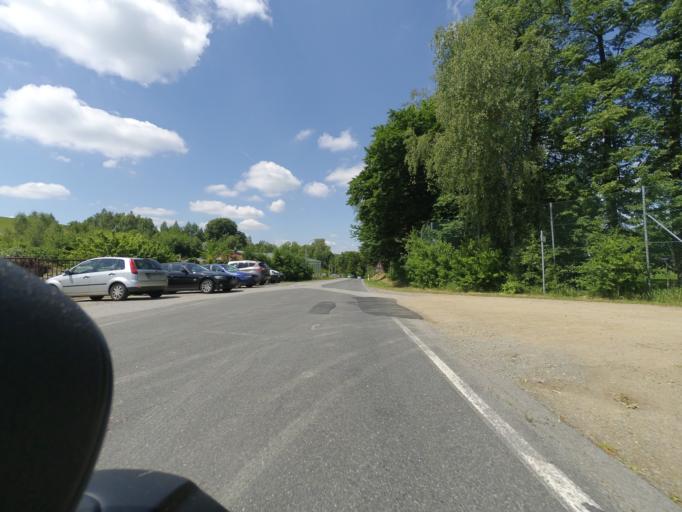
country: DE
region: Saxony
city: Hohnstein
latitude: 50.9778
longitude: 14.1239
